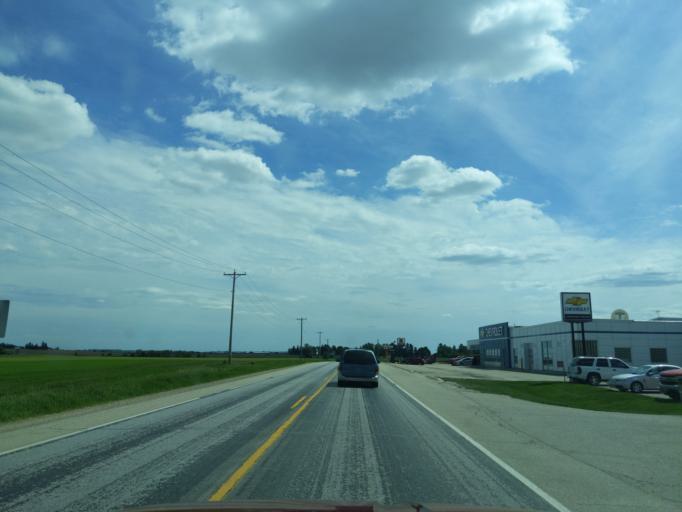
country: US
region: Wisconsin
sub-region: Dane County
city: De Forest
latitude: 43.3238
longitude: -89.3254
